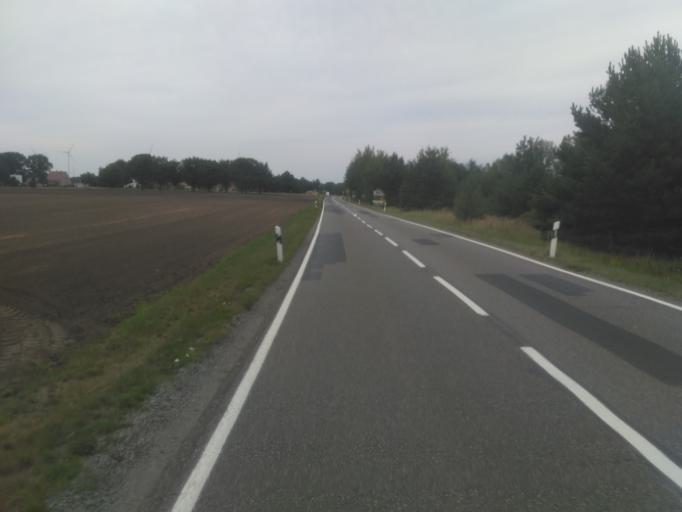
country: DE
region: Brandenburg
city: Welzow
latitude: 51.5164
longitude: 14.1783
